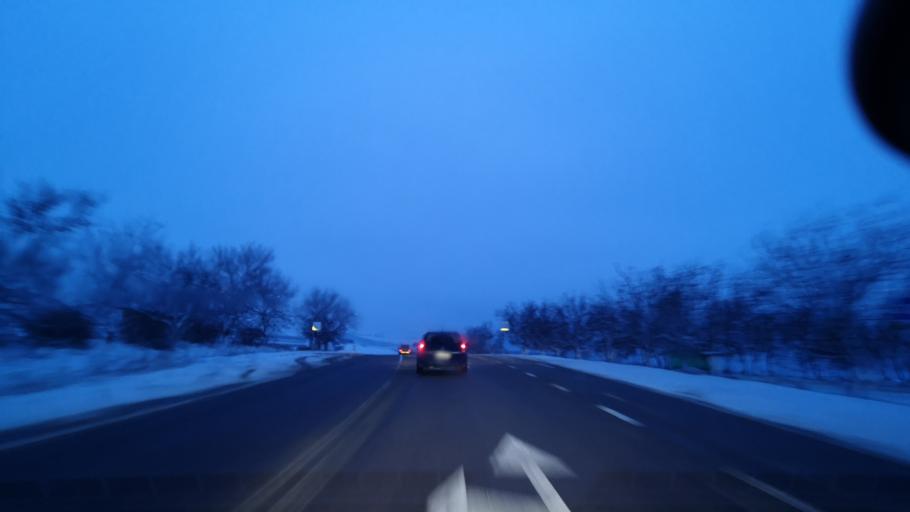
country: MD
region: Rezina
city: Saharna
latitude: 47.6265
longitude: 28.8348
